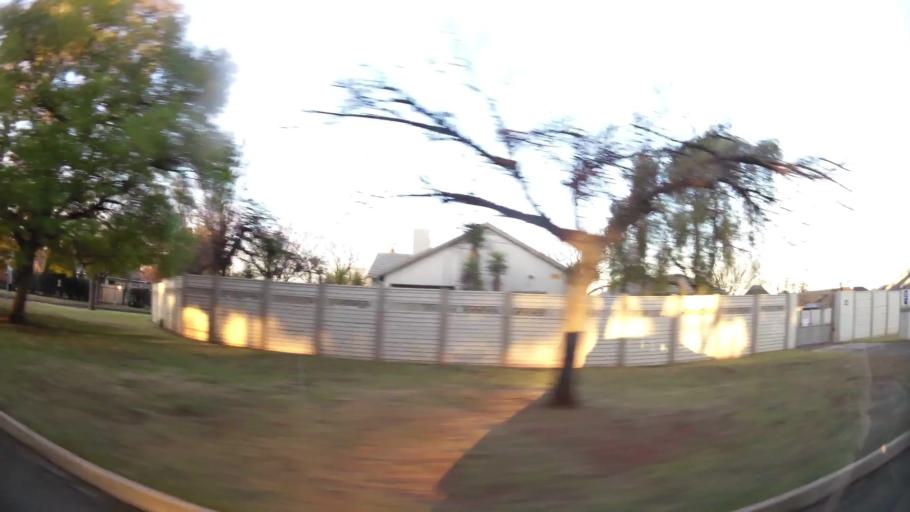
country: ZA
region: Gauteng
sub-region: City of Johannesburg Metropolitan Municipality
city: Roodepoort
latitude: -26.1535
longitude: 27.8816
